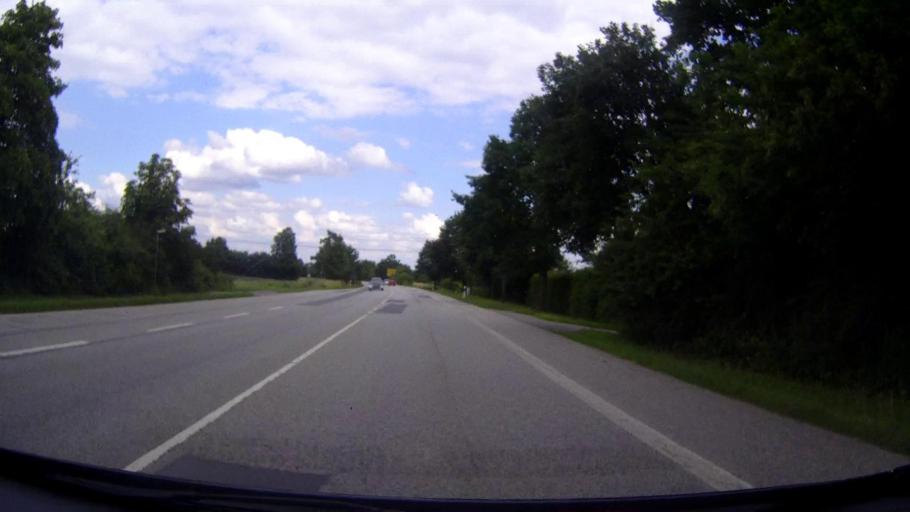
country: DE
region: Schleswig-Holstein
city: Stockelsdorf
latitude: 53.8915
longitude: 10.6116
